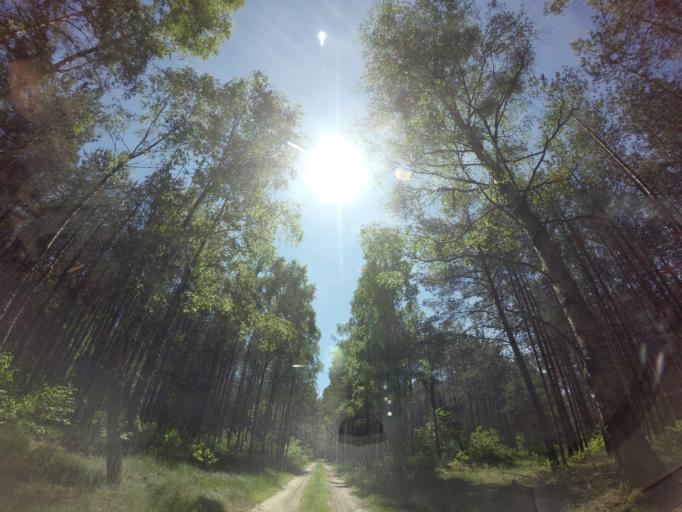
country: PL
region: West Pomeranian Voivodeship
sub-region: Powiat choszczenski
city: Drawno
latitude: 53.2469
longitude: 15.7543
